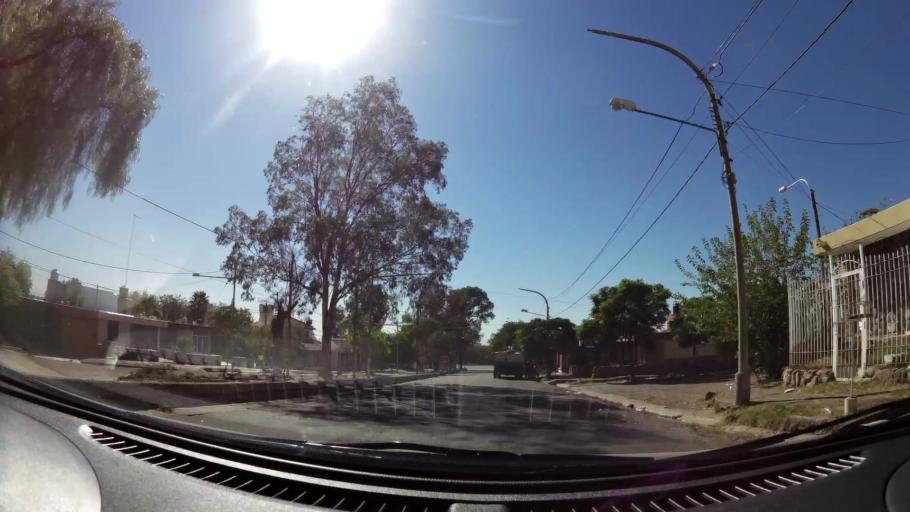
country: AR
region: Mendoza
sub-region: Departamento de Godoy Cruz
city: Godoy Cruz
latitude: -32.9039
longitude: -68.8860
